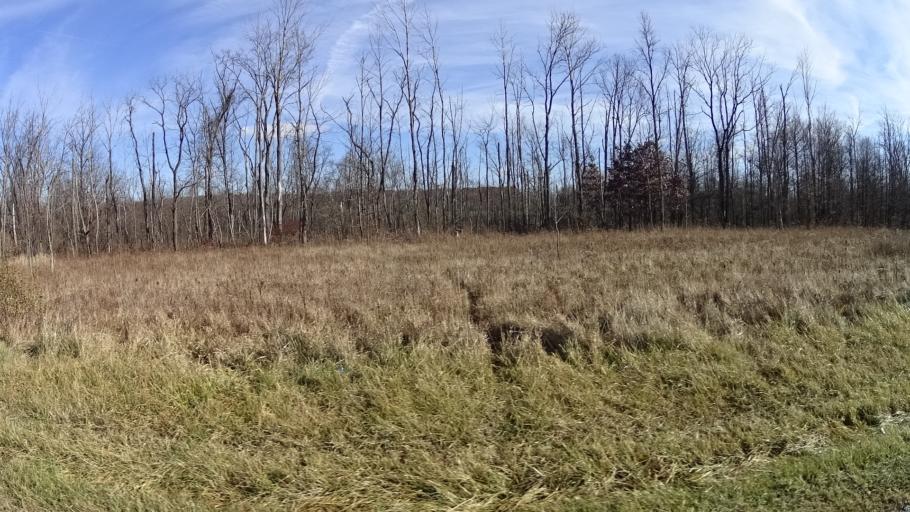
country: US
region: Ohio
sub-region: Lorain County
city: Wellington
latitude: 41.0755
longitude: -82.2592
